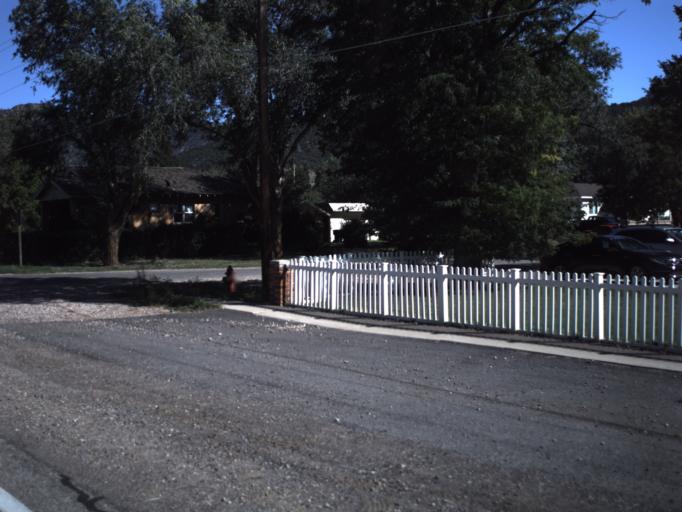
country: US
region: Utah
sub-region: Iron County
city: Parowan
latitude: 37.8388
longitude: -112.8344
